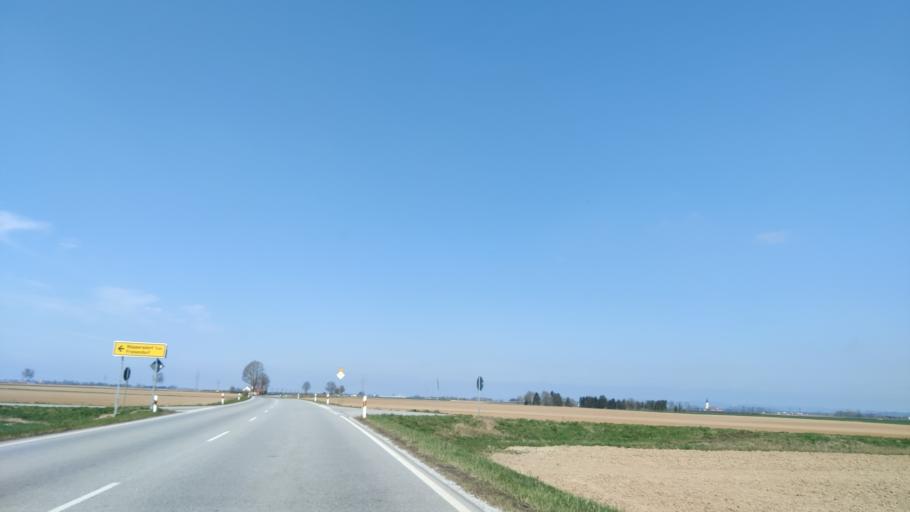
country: DE
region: Bavaria
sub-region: Lower Bavaria
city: Stephansposching
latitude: 48.8054
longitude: 12.7893
